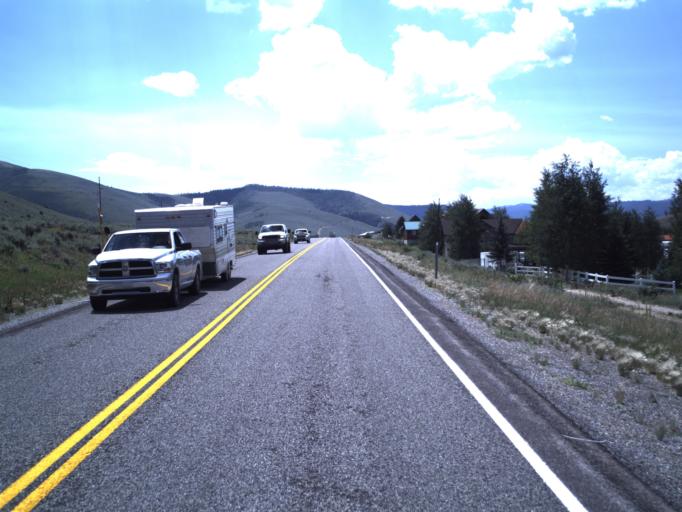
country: US
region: Utah
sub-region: Carbon County
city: Helper
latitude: 39.8063
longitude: -111.1349
